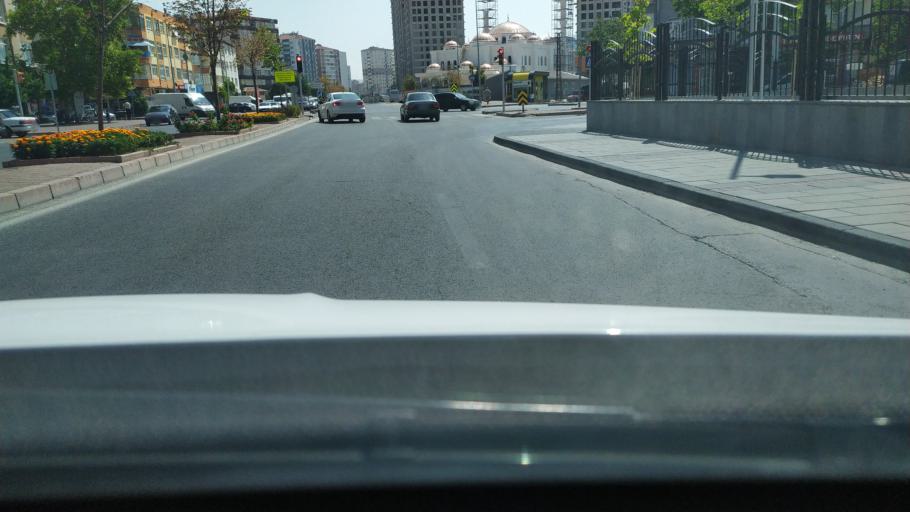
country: TR
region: Kayseri
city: Kayseri
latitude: 38.7305
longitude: 35.4880
